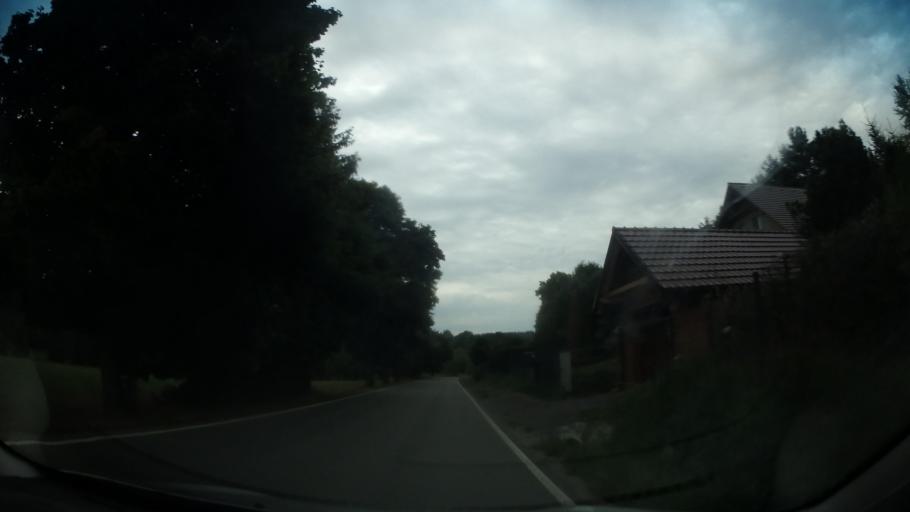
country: CZ
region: Pardubicky
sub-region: Okres Chrudim
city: Nasavrky
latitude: 49.7991
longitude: 15.7756
